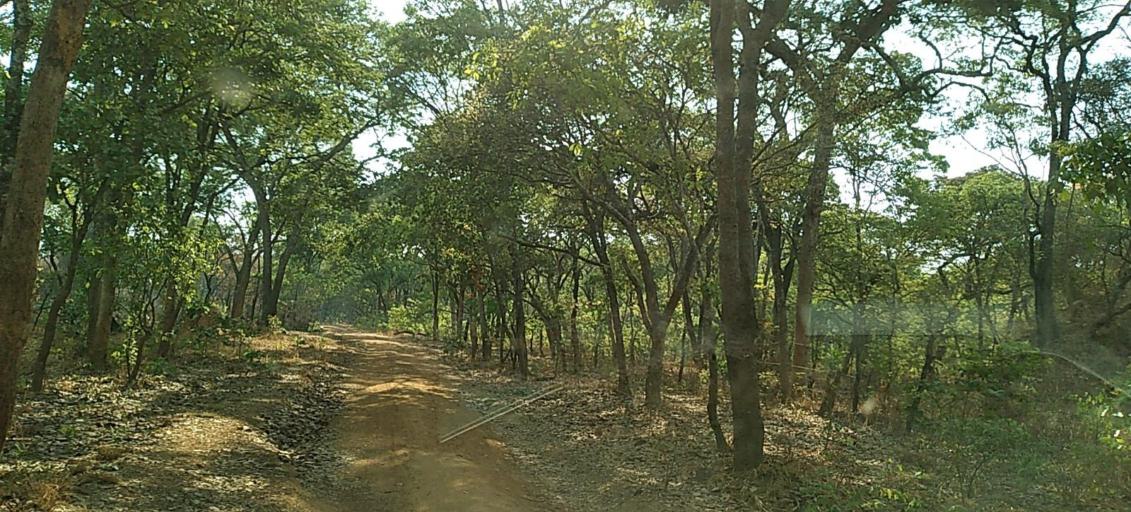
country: ZM
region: Copperbelt
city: Kalulushi
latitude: -13.0069
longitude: 27.7247
